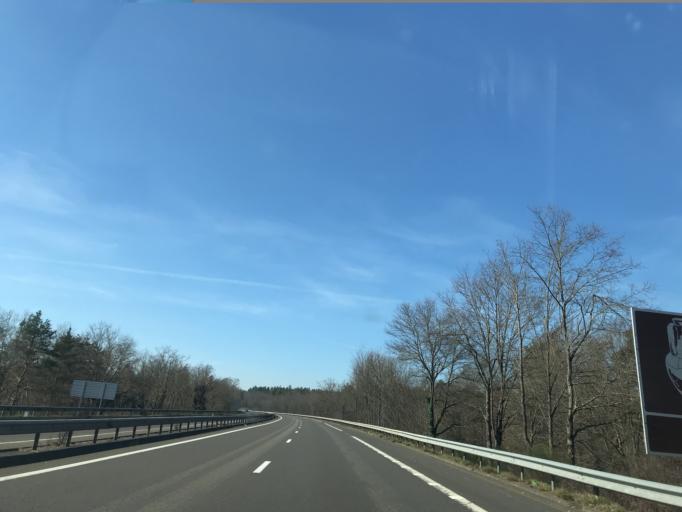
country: FR
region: Auvergne
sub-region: Departement du Puy-de-Dome
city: Orleat
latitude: 45.8550
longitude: 3.4644
